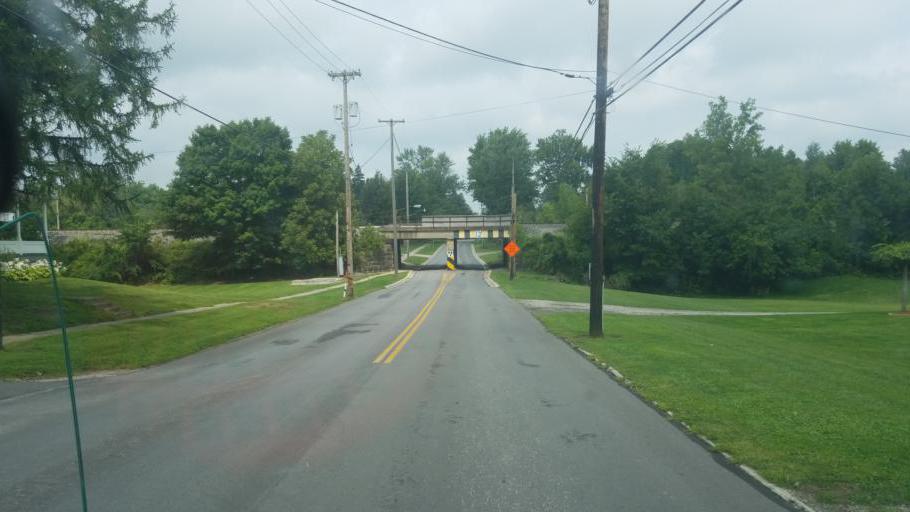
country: US
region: Ohio
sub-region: Huron County
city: Greenwich
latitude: 41.0341
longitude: -82.5165
